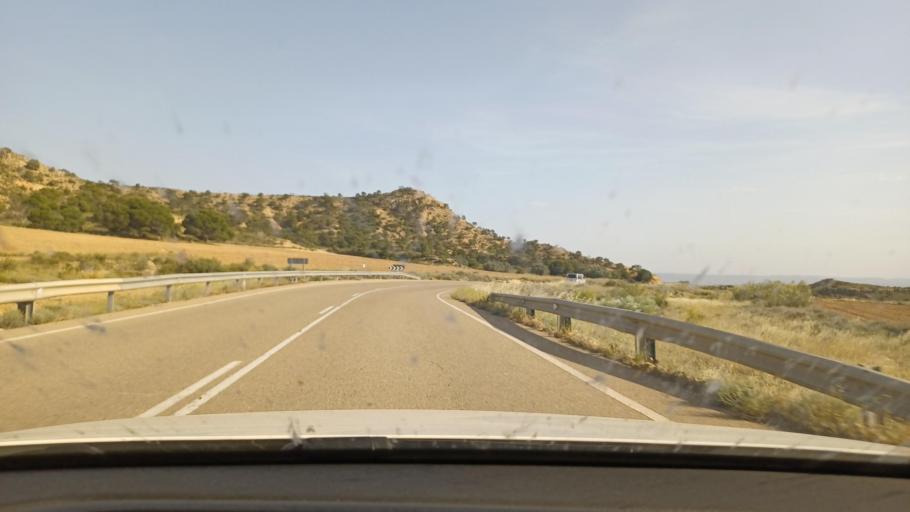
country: ES
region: Aragon
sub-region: Provincia de Zaragoza
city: Chiprana
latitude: 41.3377
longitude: -0.0891
